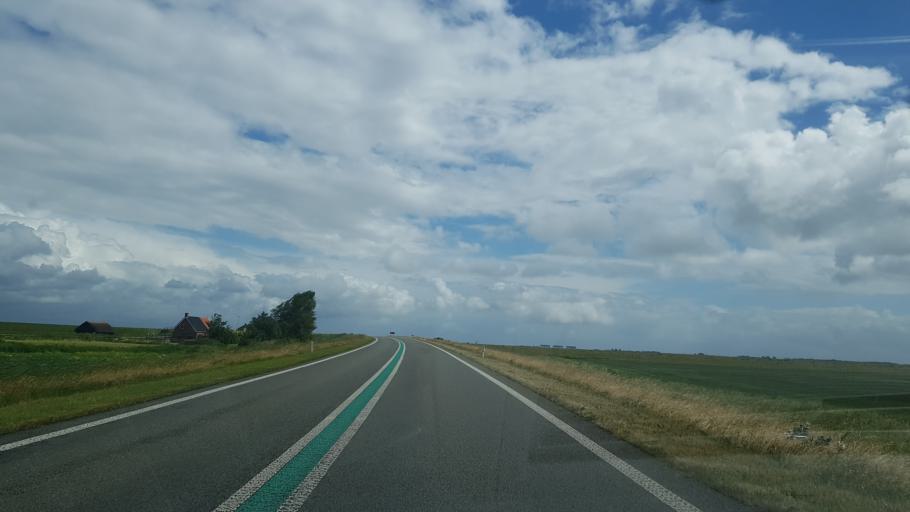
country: NL
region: Friesland
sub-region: Gemeente Dongeradeel
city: Anjum
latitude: 53.3907
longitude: 6.1467
